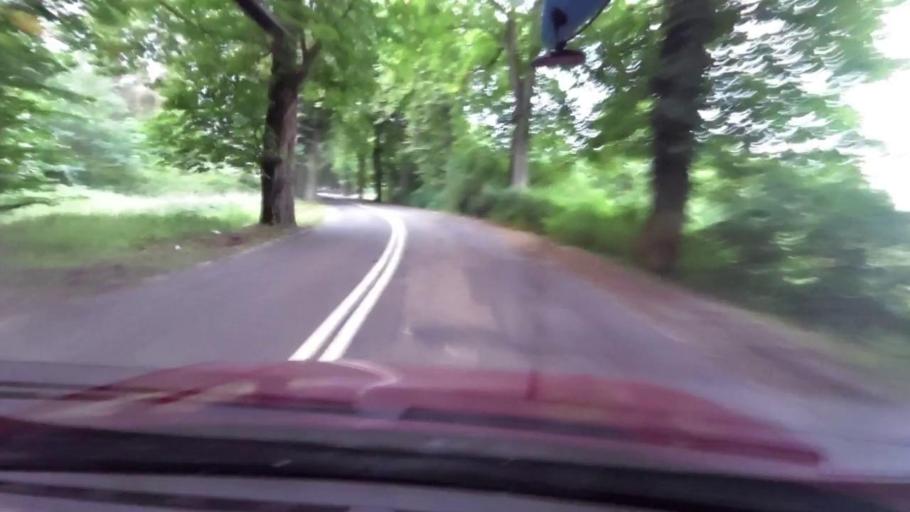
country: PL
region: West Pomeranian Voivodeship
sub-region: Powiat koszalinski
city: Sianow
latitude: 54.1873
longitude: 16.2461
